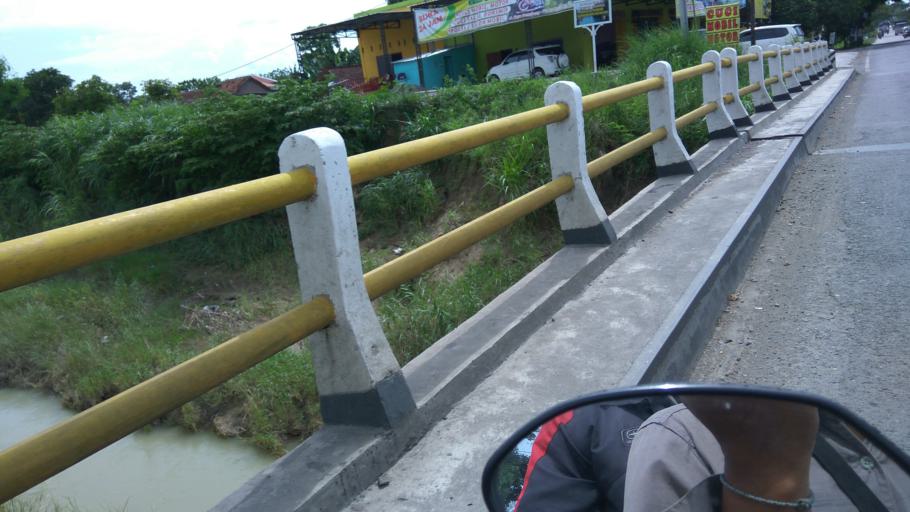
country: ID
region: Central Java
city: Mranggen
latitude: -7.0476
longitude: 110.5897
